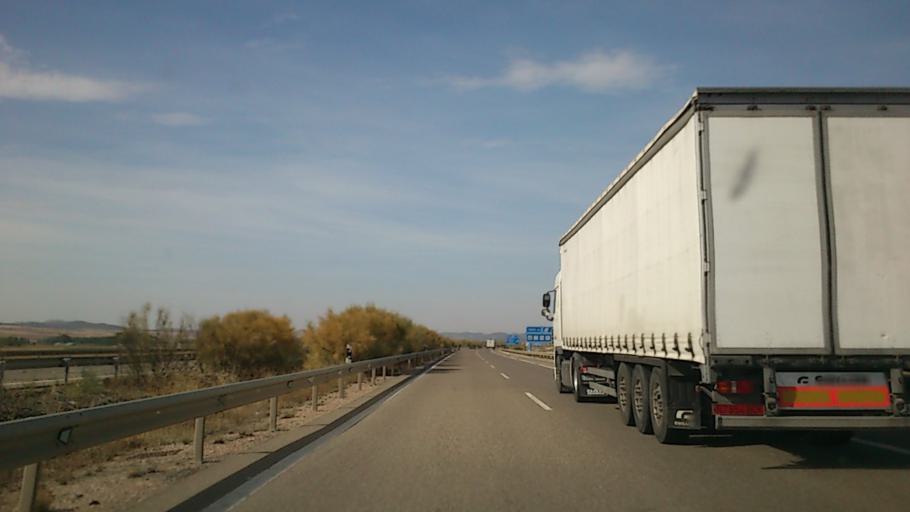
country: ES
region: Aragon
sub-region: Provincia de Teruel
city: Fuentes Claras
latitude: 40.8711
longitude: -1.3072
